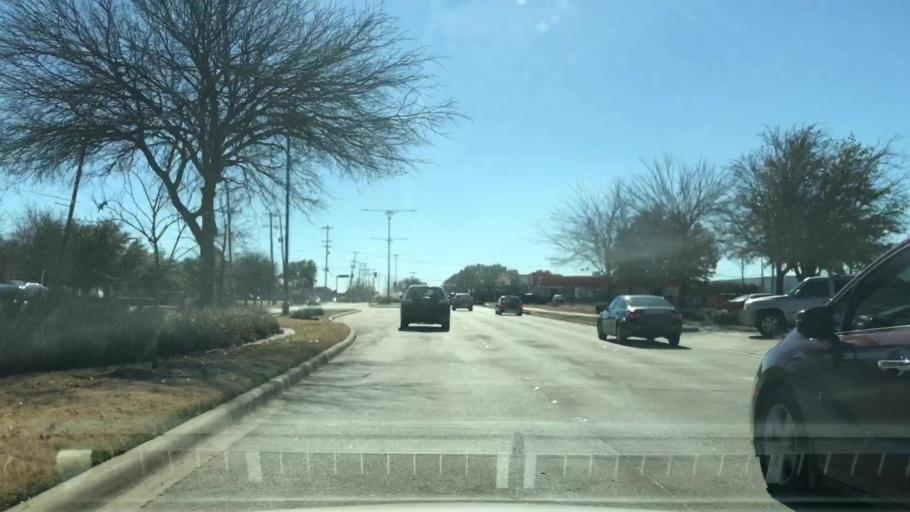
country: US
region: Texas
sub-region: Dallas County
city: Coppell
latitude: 32.9499
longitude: -96.9936
